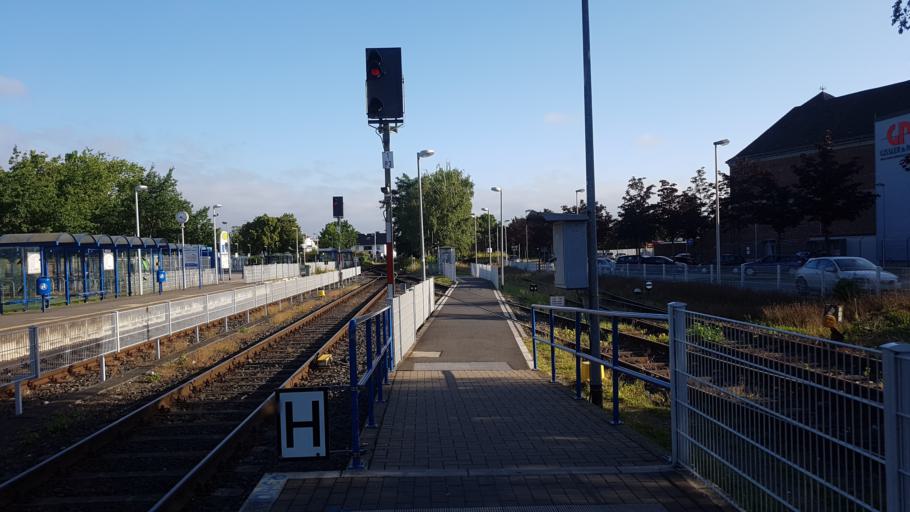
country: DE
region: North Rhine-Westphalia
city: Julich
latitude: 50.9185
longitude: 6.3683
